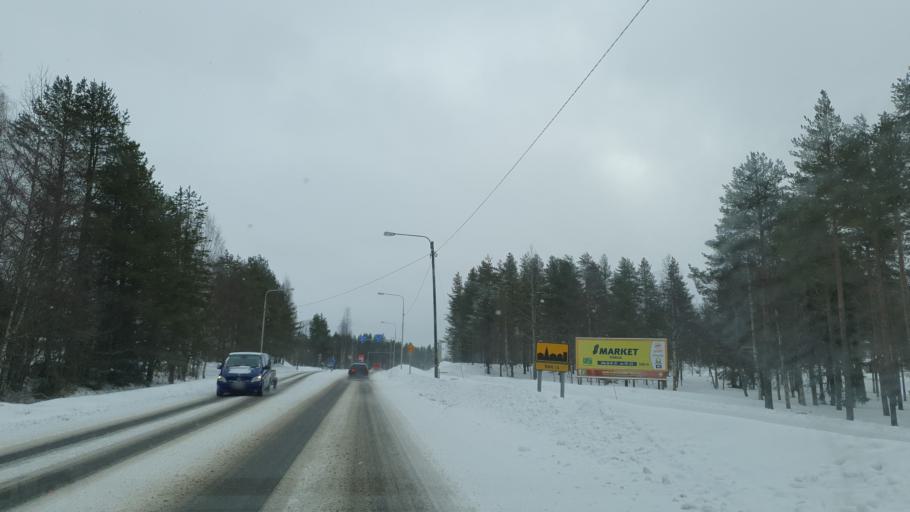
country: FI
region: Lapland
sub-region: Rovaniemi
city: Ranua
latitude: 65.9331
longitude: 26.5003
